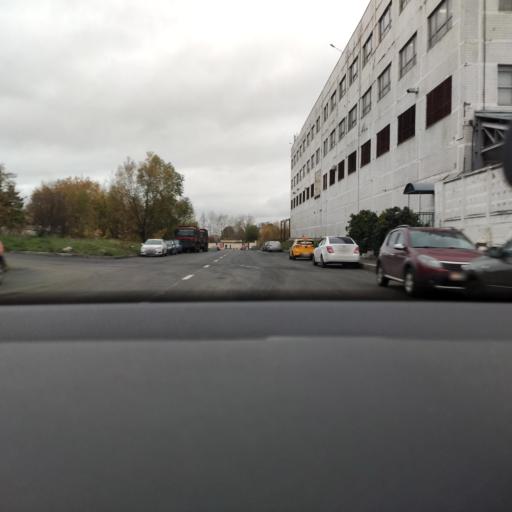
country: RU
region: Moscow
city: Mikhalkovo
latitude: 55.6764
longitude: 37.4285
